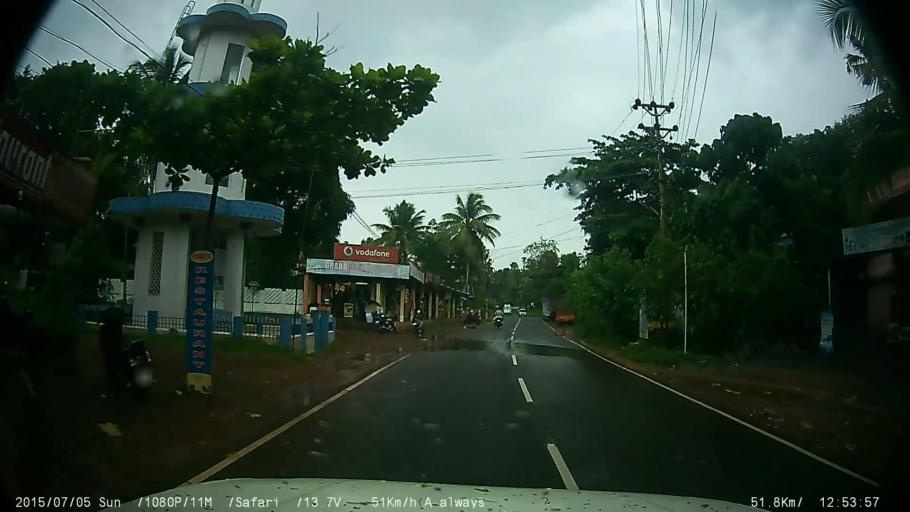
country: IN
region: Kerala
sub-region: Kottayam
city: Changanacheri
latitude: 9.4449
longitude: 76.5707
